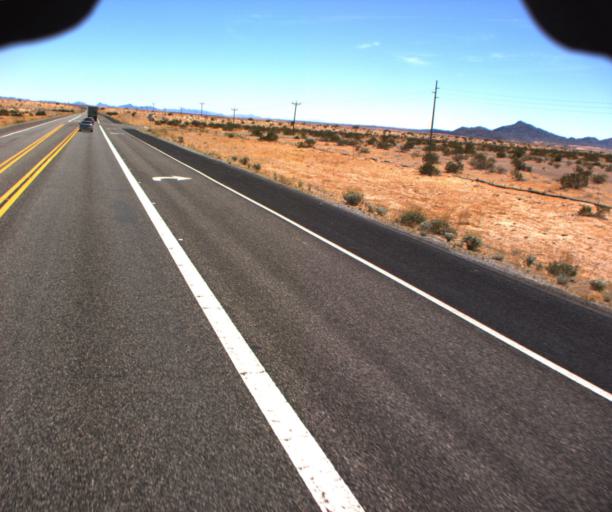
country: US
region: Arizona
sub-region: La Paz County
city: Parker
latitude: 34.0876
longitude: -114.2729
